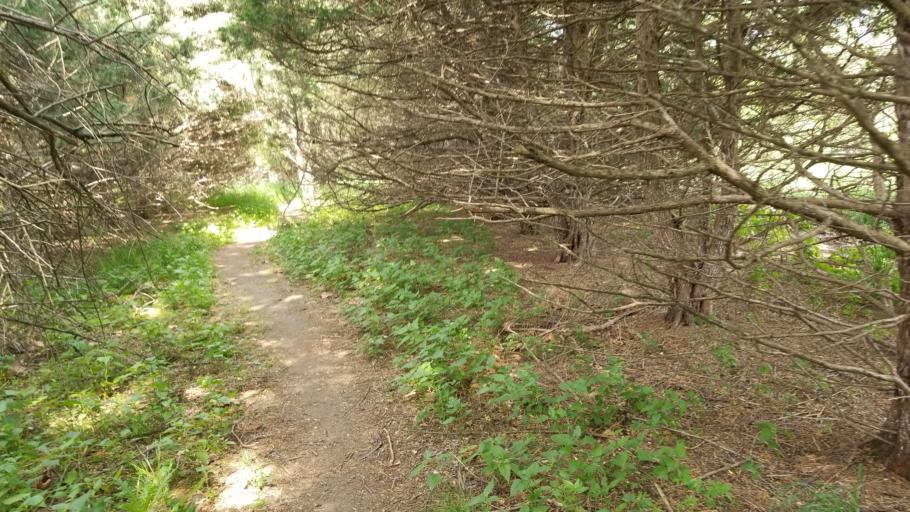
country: US
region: Nebraska
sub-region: Sarpy County
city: Chalco
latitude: 41.1728
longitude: -96.1635
